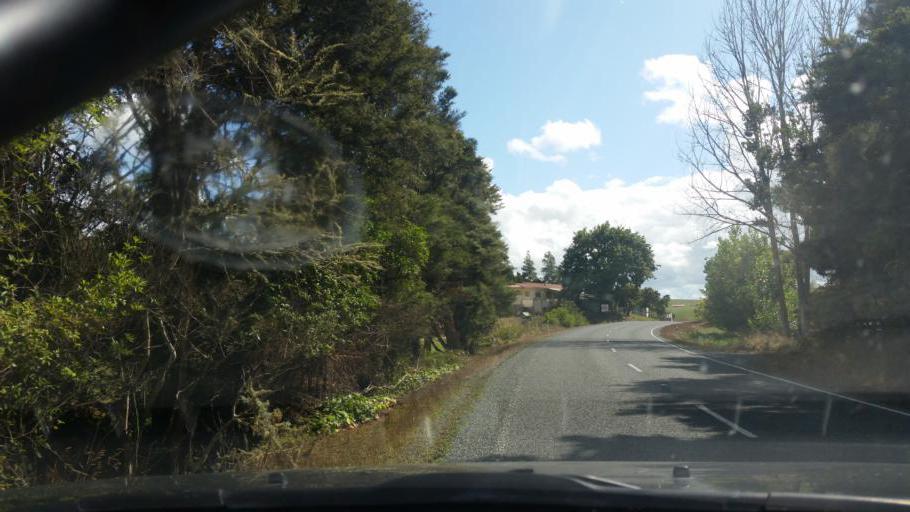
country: NZ
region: Northland
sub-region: Whangarei
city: Ruakaka
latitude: -36.0287
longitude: 174.2772
